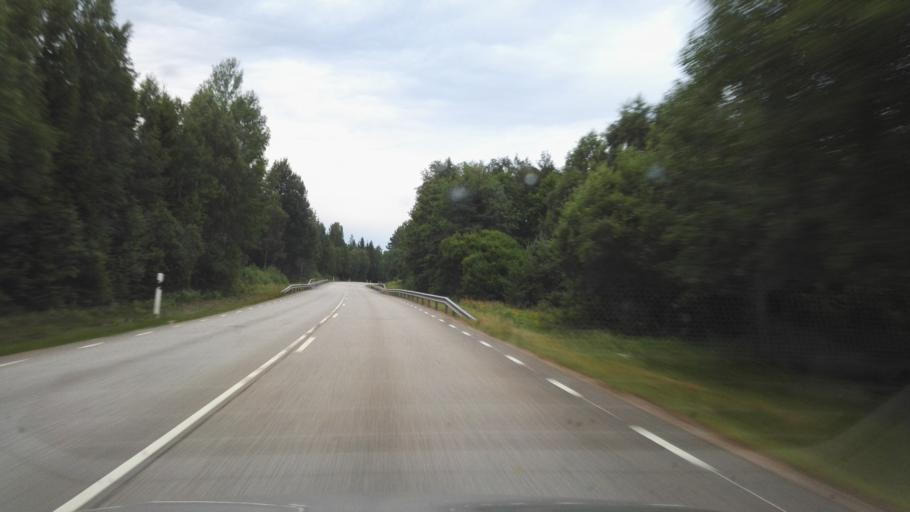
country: SE
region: Kronoberg
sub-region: Vaxjo Kommun
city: Braas
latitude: 57.0395
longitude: 15.0665
